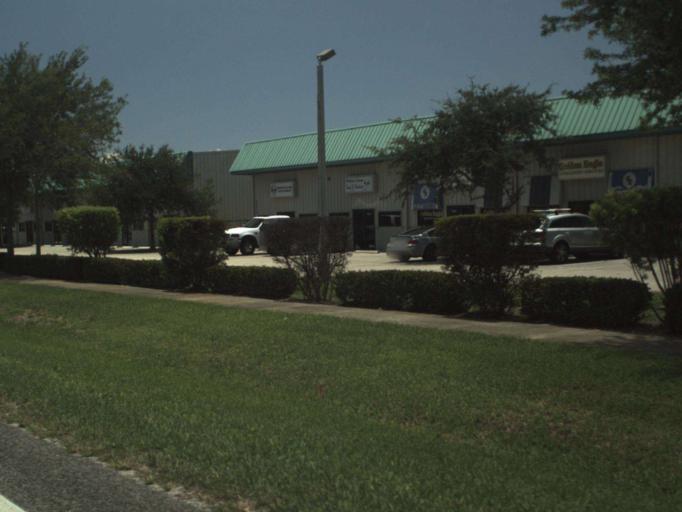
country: US
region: Florida
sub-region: Indian River County
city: Gifford
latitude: 27.6949
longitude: -80.4142
